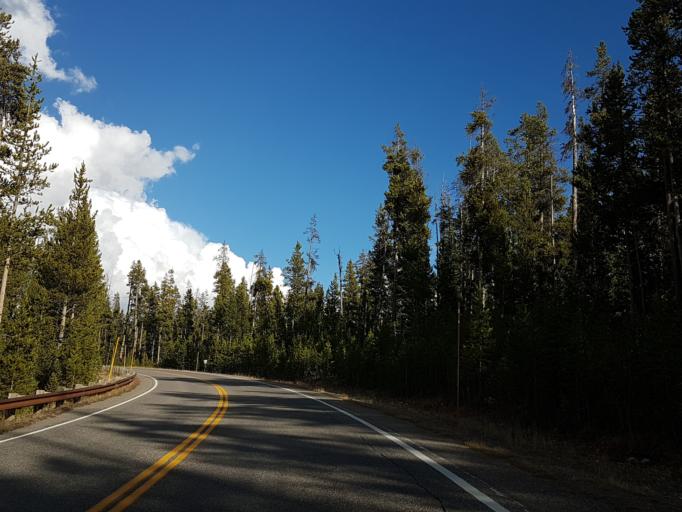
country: US
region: Montana
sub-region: Gallatin County
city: West Yellowstone
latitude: 44.4466
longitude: -110.7004
